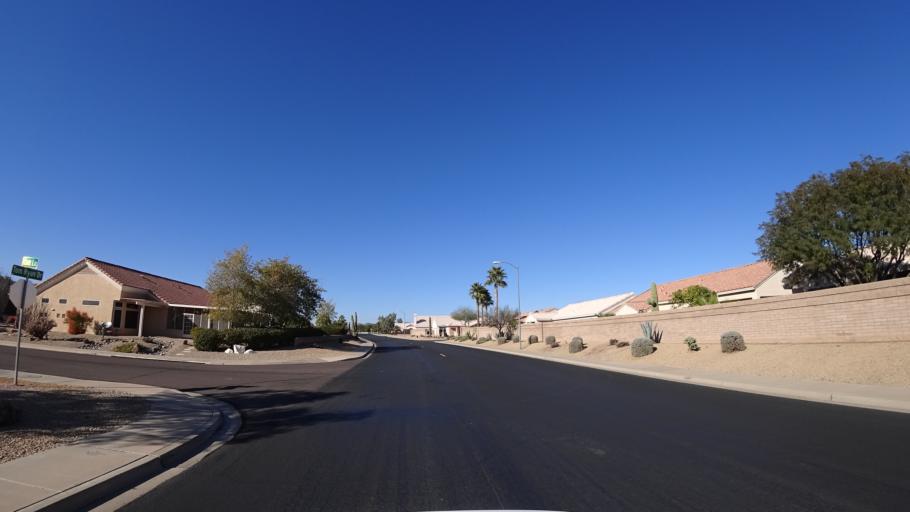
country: US
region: Arizona
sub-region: Maricopa County
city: Sun City West
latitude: 33.6895
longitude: -112.3682
